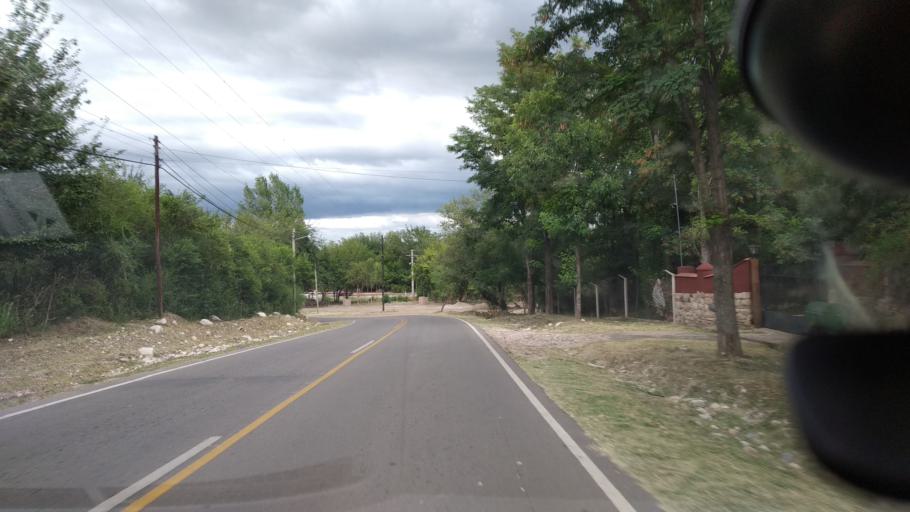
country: AR
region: Cordoba
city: Villa Las Rosas
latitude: -31.9372
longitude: -65.0402
